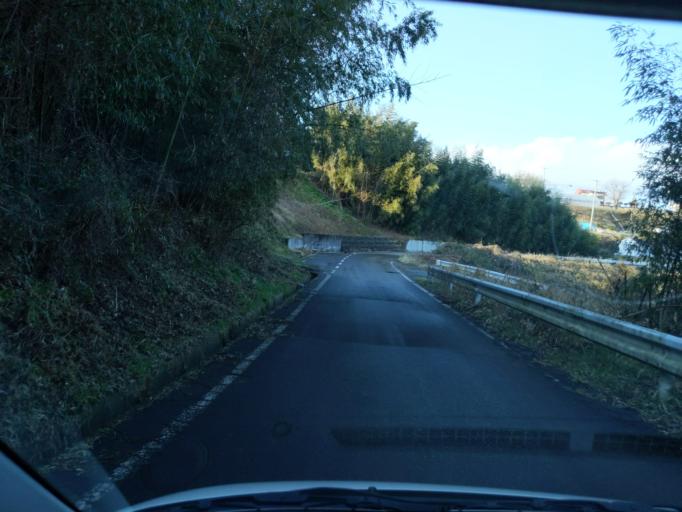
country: JP
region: Miyagi
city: Wakuya
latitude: 38.7072
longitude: 141.1399
